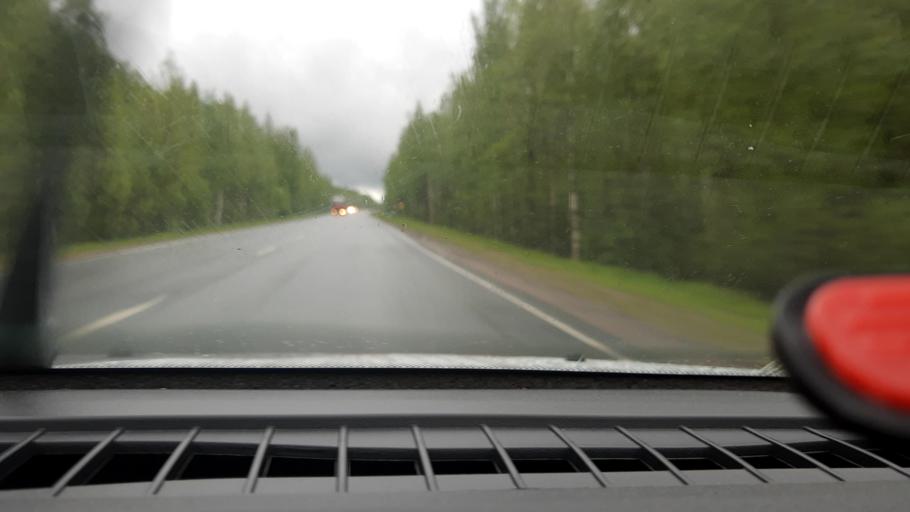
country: RU
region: Nizjnij Novgorod
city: Semenov
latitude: 56.7806
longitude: 44.4332
